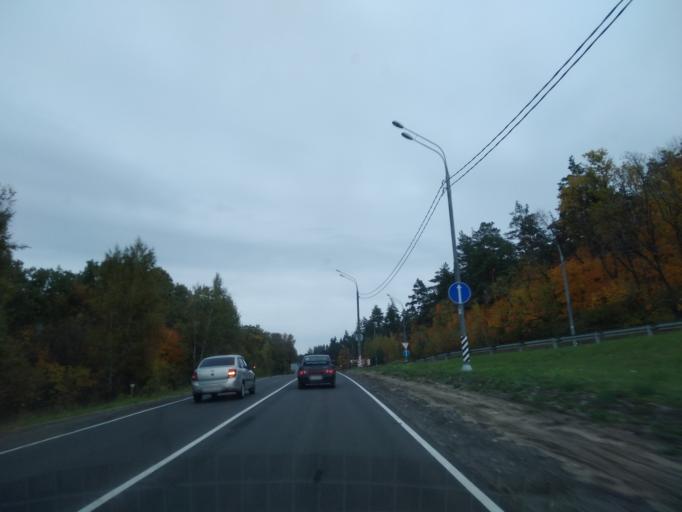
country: RU
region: Lipetsk
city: Zadonsk
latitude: 52.3700
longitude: 38.9178
